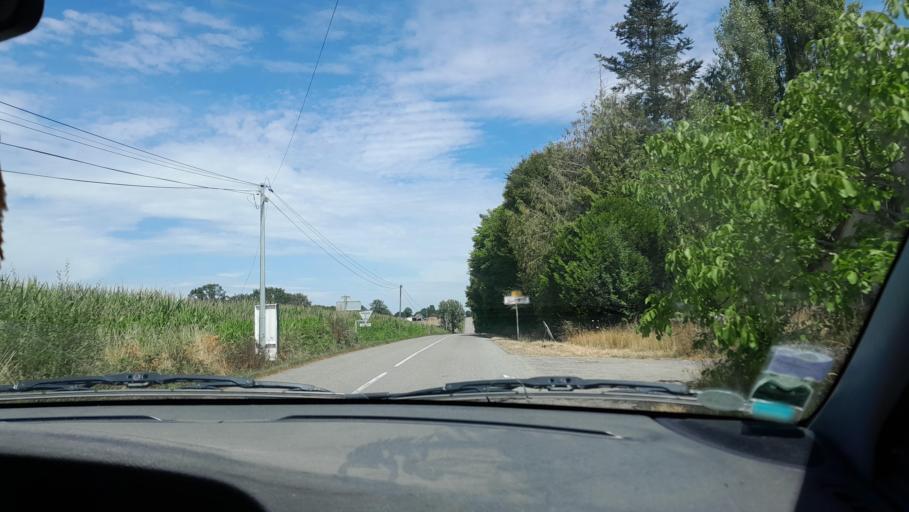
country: FR
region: Brittany
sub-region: Departement d'Ille-et-Vilaine
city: Le Pertre
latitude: 47.9672
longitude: -1.0418
